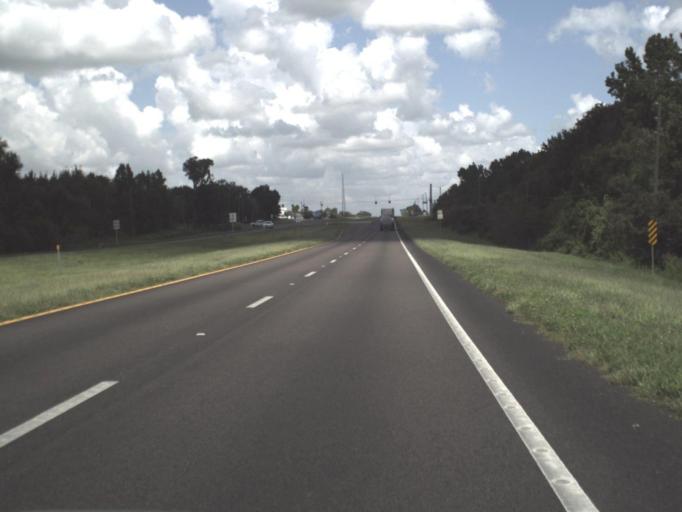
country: US
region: Florida
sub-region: Hardee County
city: Bowling Green
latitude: 27.5924
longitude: -81.8213
